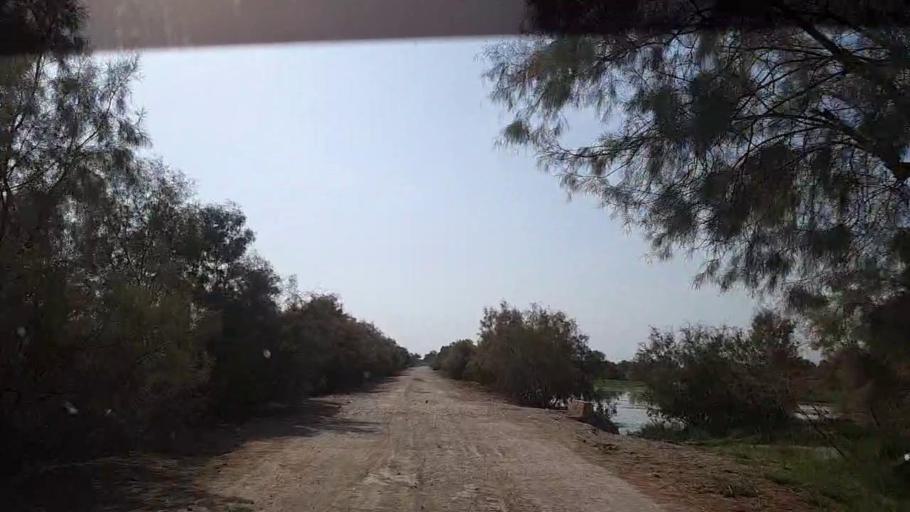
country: PK
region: Sindh
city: Khanpur
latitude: 27.8389
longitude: 69.3169
